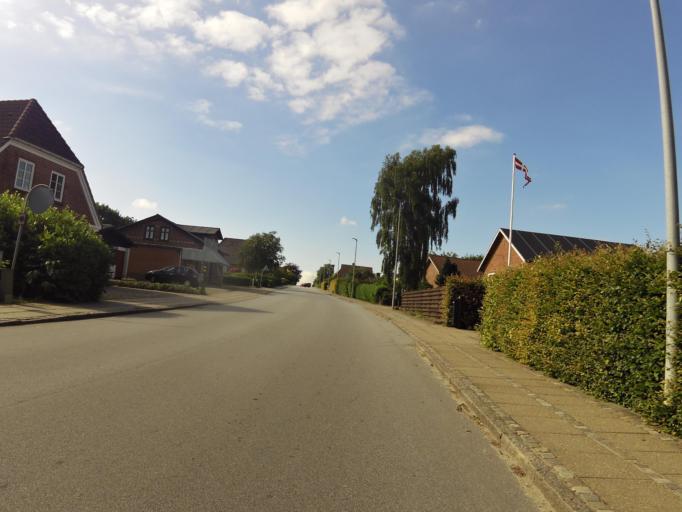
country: DK
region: South Denmark
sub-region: Vejen Kommune
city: Rodding
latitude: 55.3708
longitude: 9.0598
